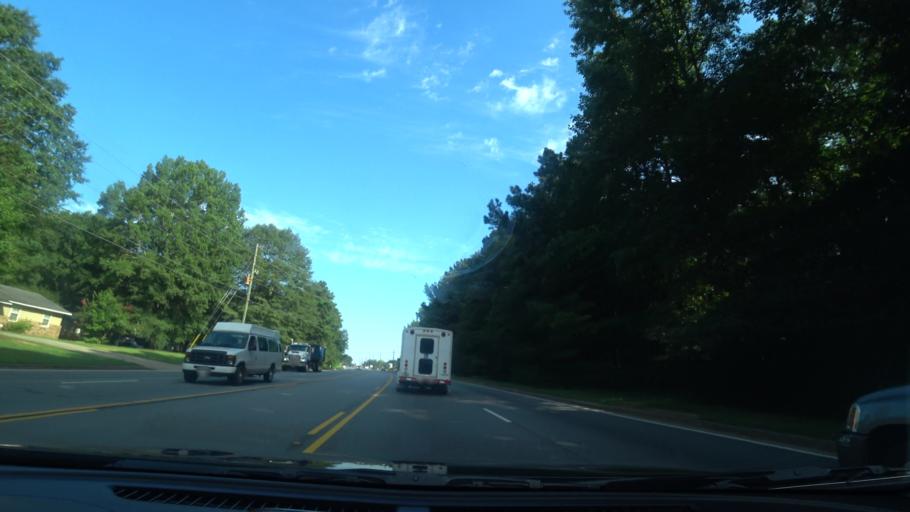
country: US
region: Georgia
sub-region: Gwinnett County
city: Lawrenceville
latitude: 33.9300
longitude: -83.9758
